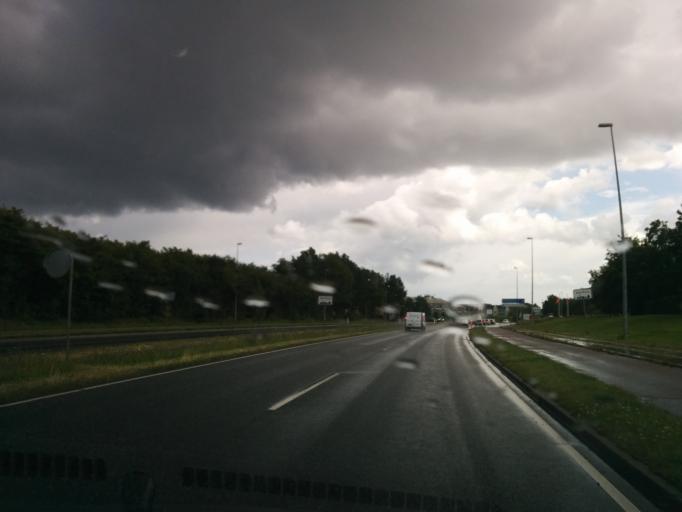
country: DK
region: Central Jutland
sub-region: Arhus Kommune
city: Arhus
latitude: 56.1883
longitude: 10.1925
